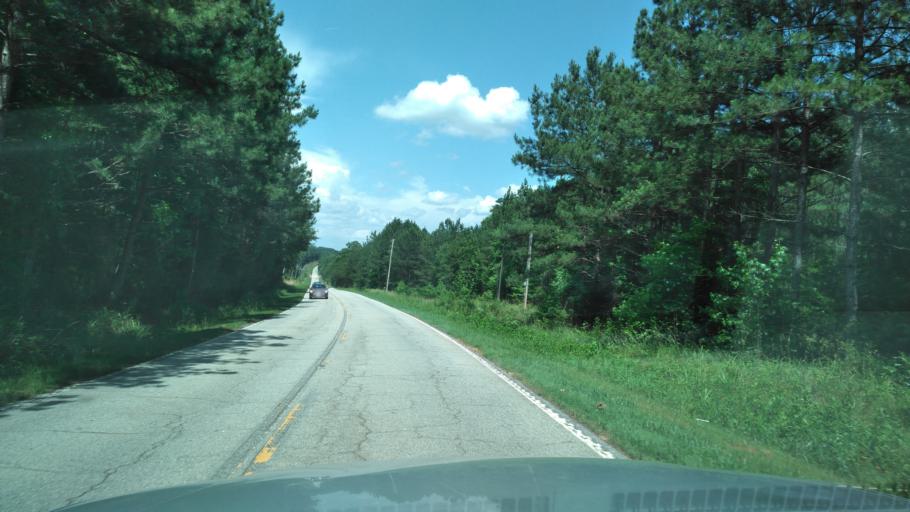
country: US
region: South Carolina
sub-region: Greenwood County
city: Ware Shoals
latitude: 34.4693
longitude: -82.1485
